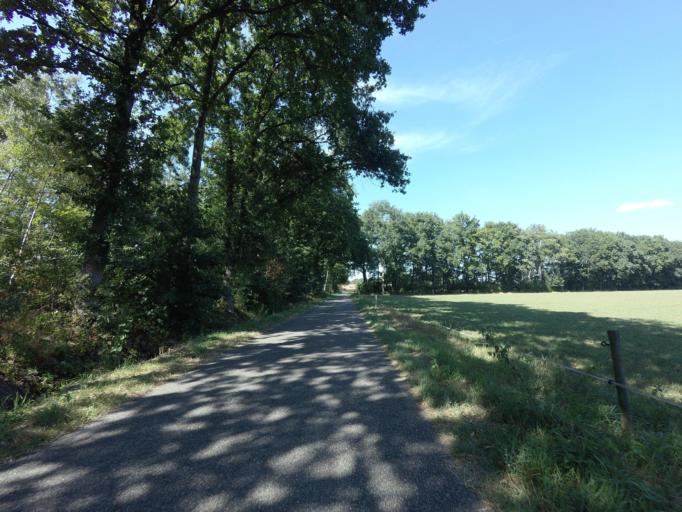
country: NL
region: Gelderland
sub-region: Gemeente Apeldoorn
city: Loenen
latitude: 52.1313
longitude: 6.0317
